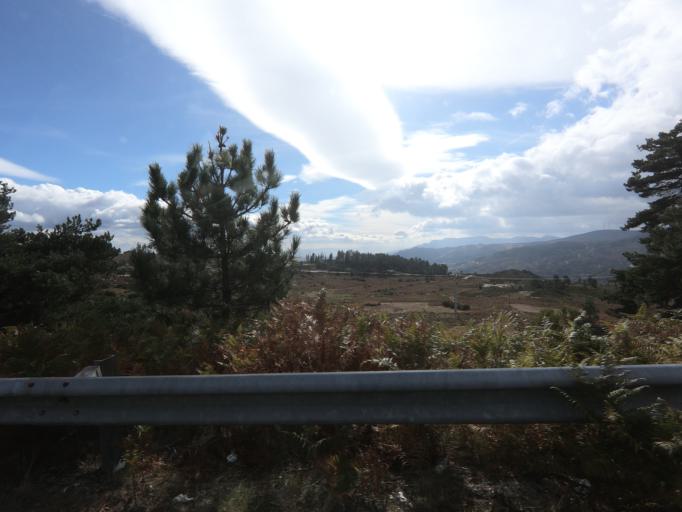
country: PT
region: Vila Real
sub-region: Vila Real
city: Vila Real
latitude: 41.3453
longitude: -7.7877
